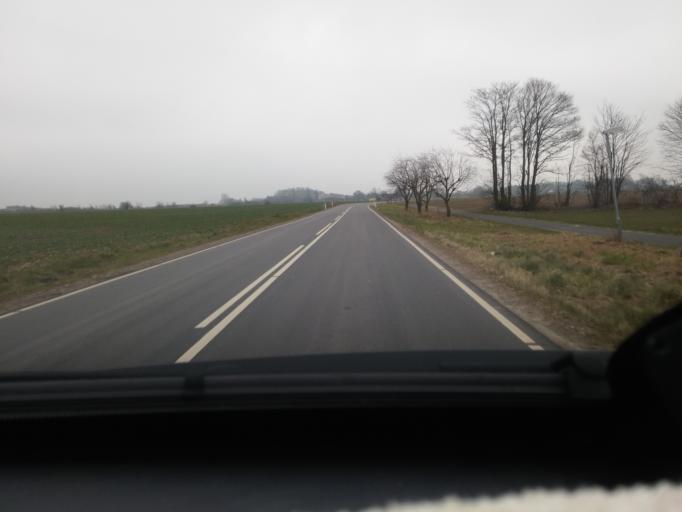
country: DK
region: South Denmark
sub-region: Nyborg Kommune
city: Ullerslev
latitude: 55.3768
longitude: 10.7263
